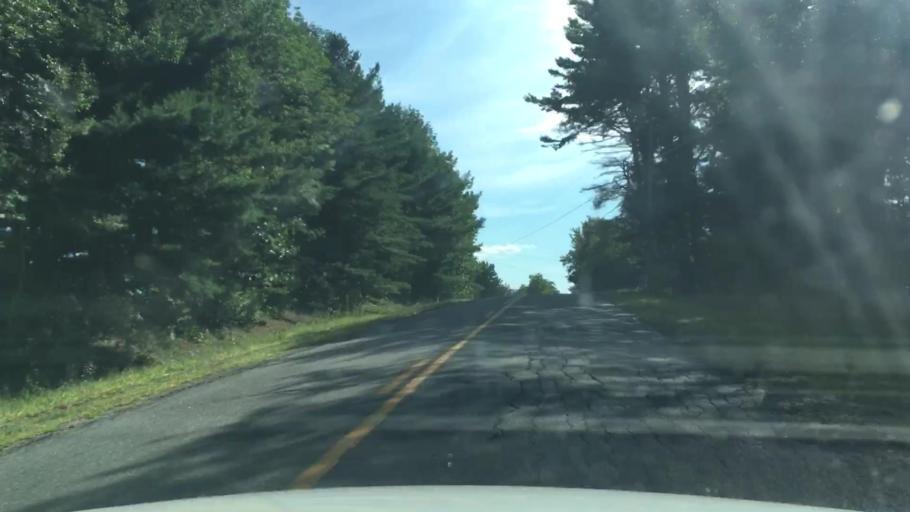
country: US
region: Maine
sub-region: Penobscot County
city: Enfield
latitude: 45.3030
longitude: -68.5482
